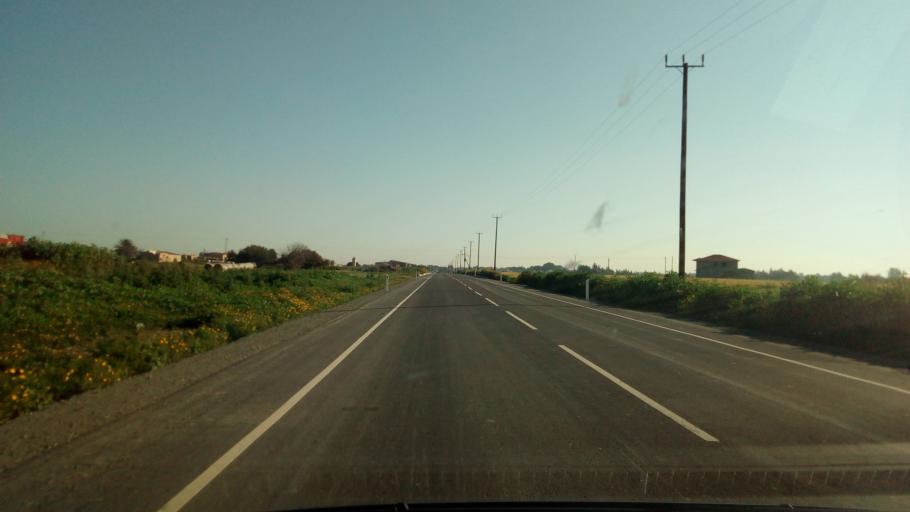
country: CY
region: Larnaka
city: Tersefanou
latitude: 34.8346
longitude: 33.5494
